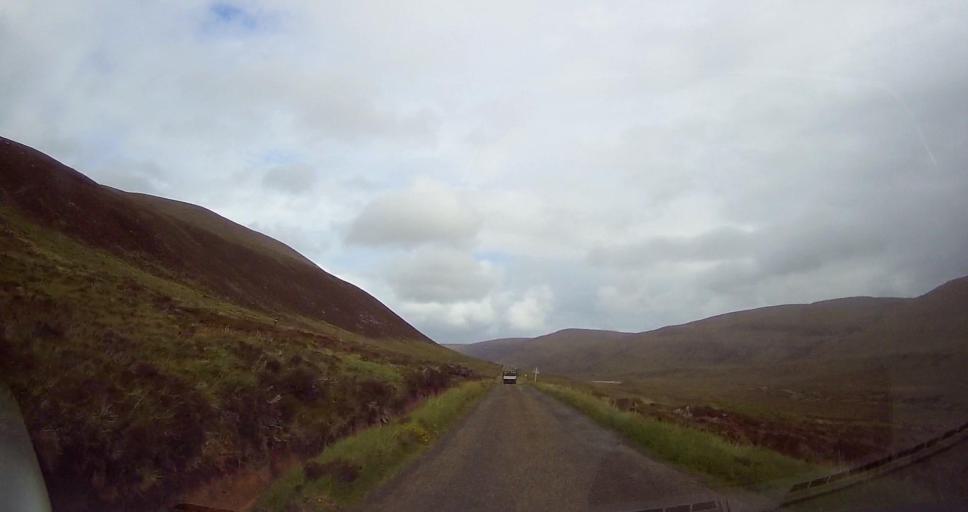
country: GB
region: Scotland
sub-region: Orkney Islands
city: Stromness
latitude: 58.8815
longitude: -3.3724
